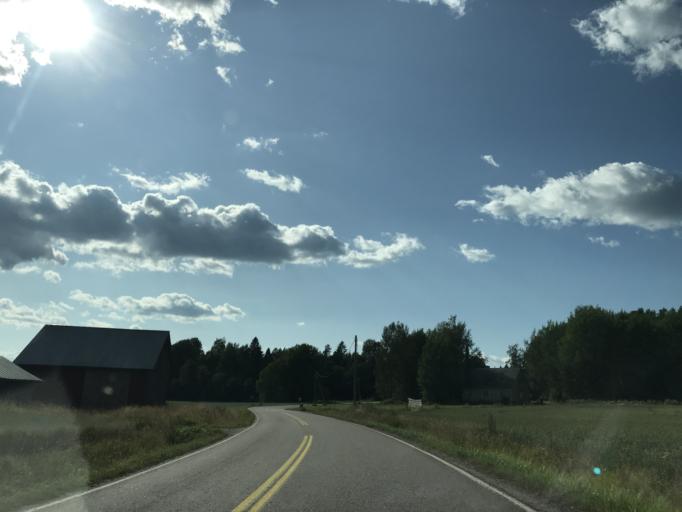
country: FI
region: Uusimaa
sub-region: Helsinki
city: Nurmijaervi
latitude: 60.4526
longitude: 24.6170
